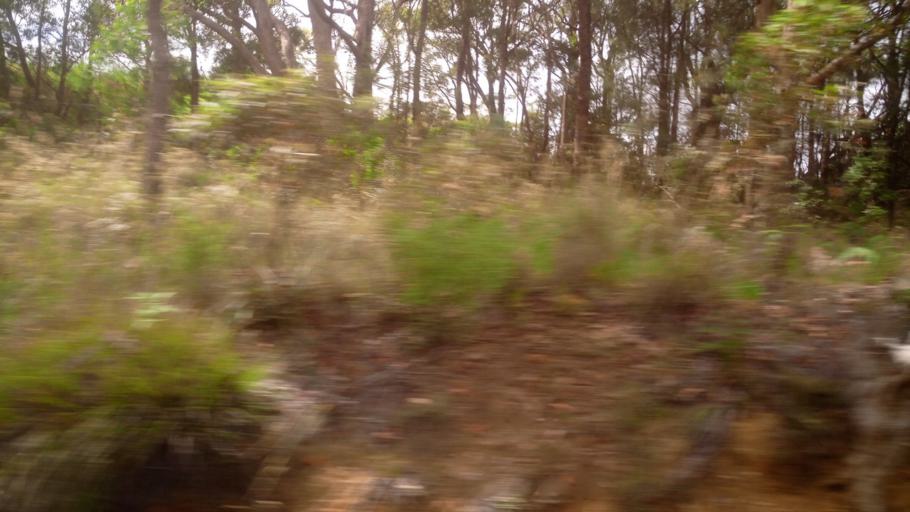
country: AU
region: New South Wales
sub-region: Blue Mountains Municipality
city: Lawson
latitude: -33.7235
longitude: 150.4049
